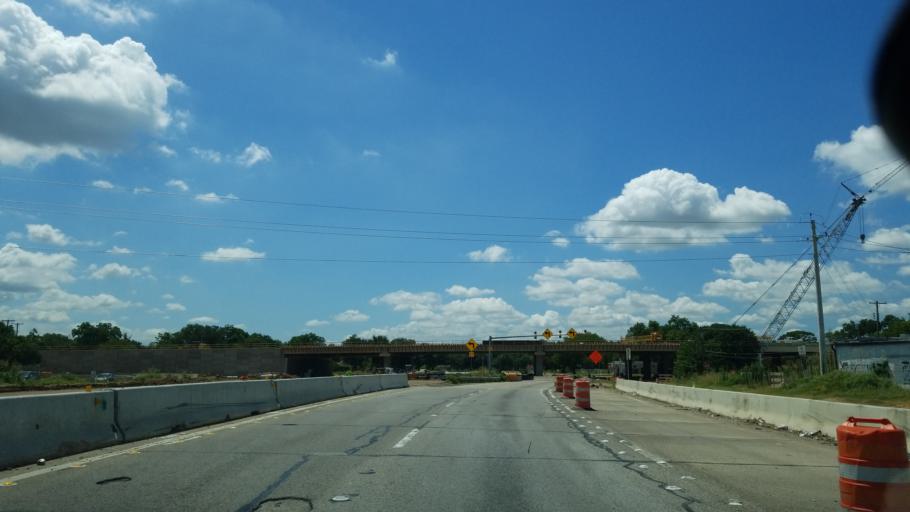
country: US
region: Texas
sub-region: Dallas County
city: Dallas
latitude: 32.7474
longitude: -96.7595
